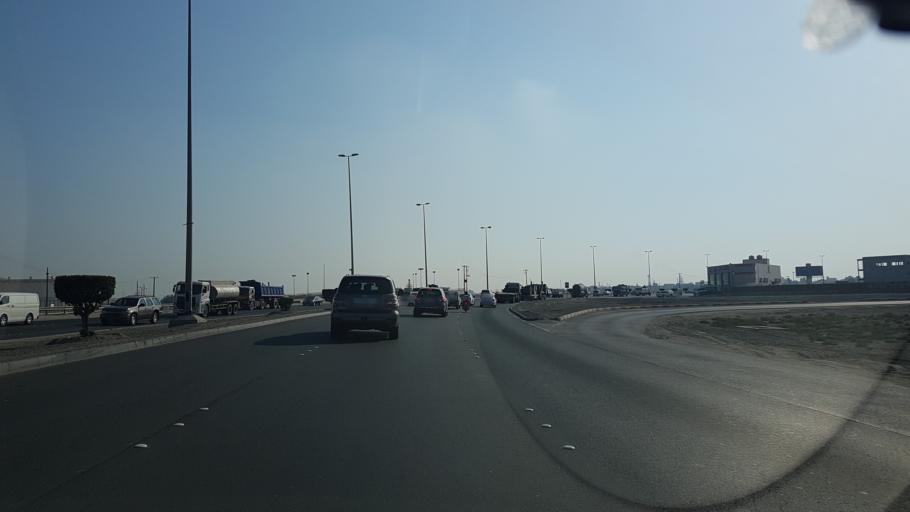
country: BH
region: Northern
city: Sitrah
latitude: 26.1458
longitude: 50.6191
